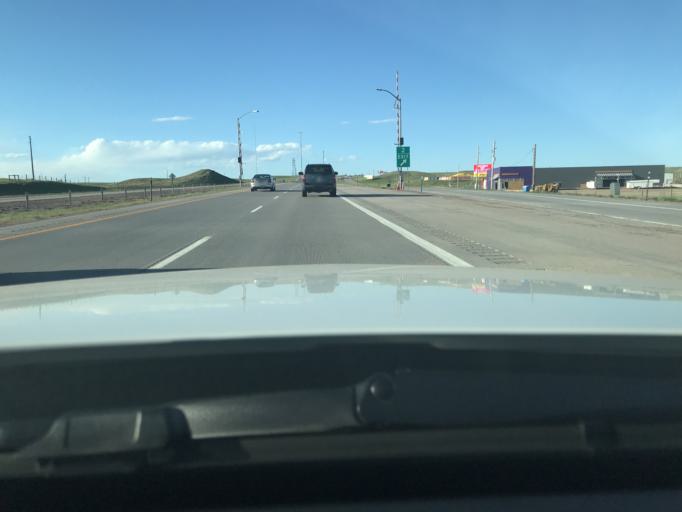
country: US
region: Wyoming
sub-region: Laramie County
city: South Greeley
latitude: 41.0320
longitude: -104.8984
